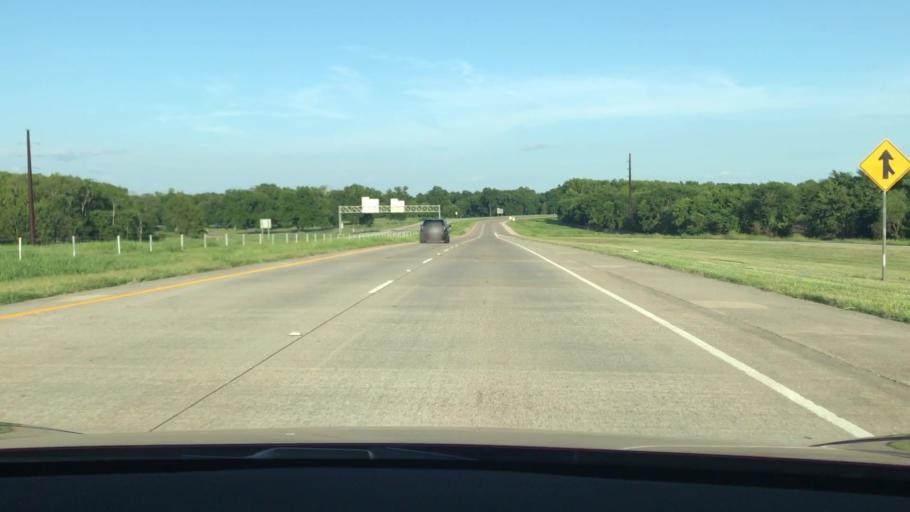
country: US
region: Louisiana
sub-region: Bossier Parish
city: Bossier City
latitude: 32.4108
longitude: -93.7229
